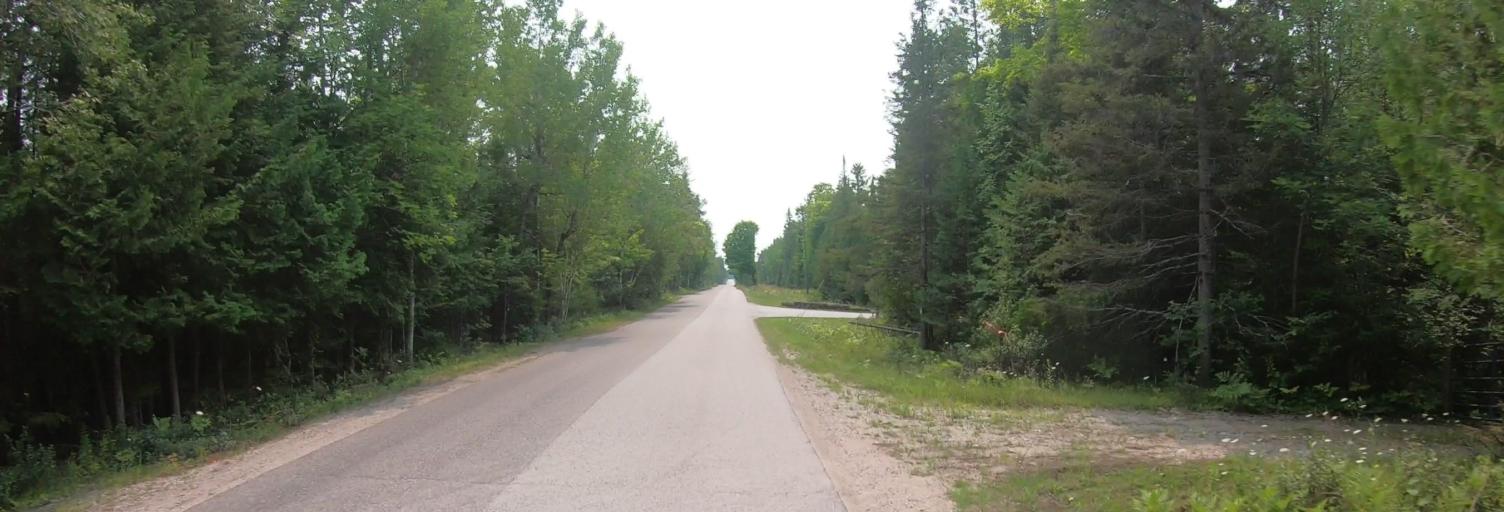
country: CA
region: Ontario
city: Thessalon
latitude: 46.0534
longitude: -83.6656
